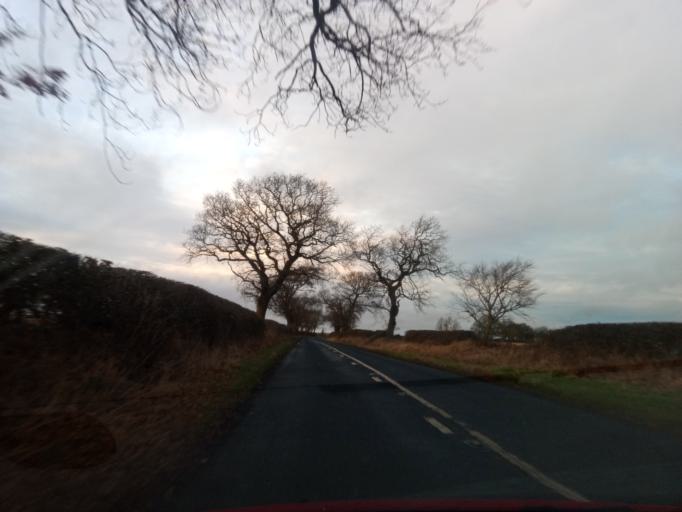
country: GB
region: England
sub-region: Northumberland
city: Meldon
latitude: 55.1254
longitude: -1.7502
